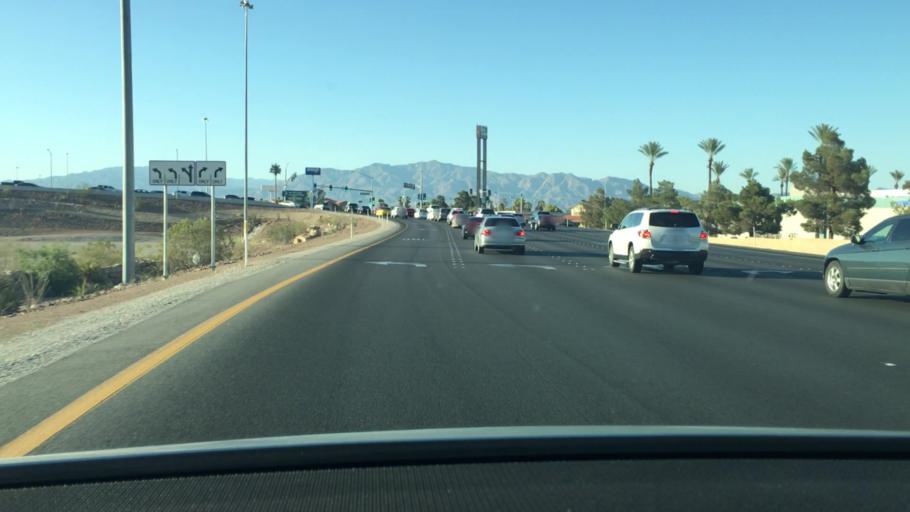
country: US
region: Nevada
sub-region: Clark County
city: Spring Valley
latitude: 36.2166
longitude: -115.2459
